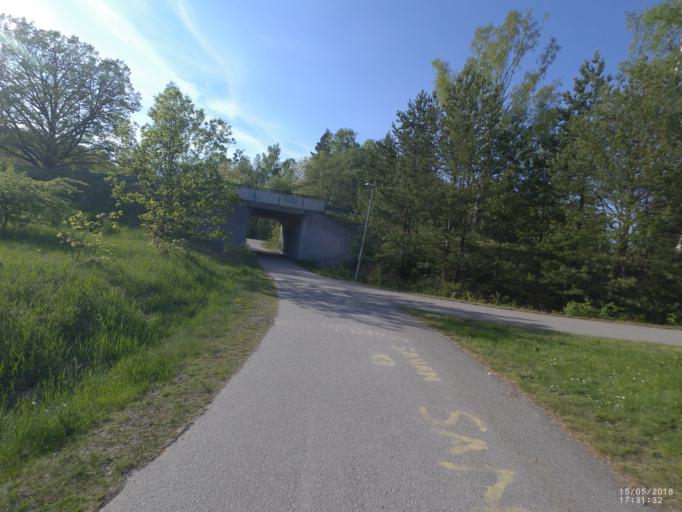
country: SE
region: Soedermanland
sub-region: Nykopings Kommun
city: Nykoping
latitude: 58.7341
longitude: 17.0168
